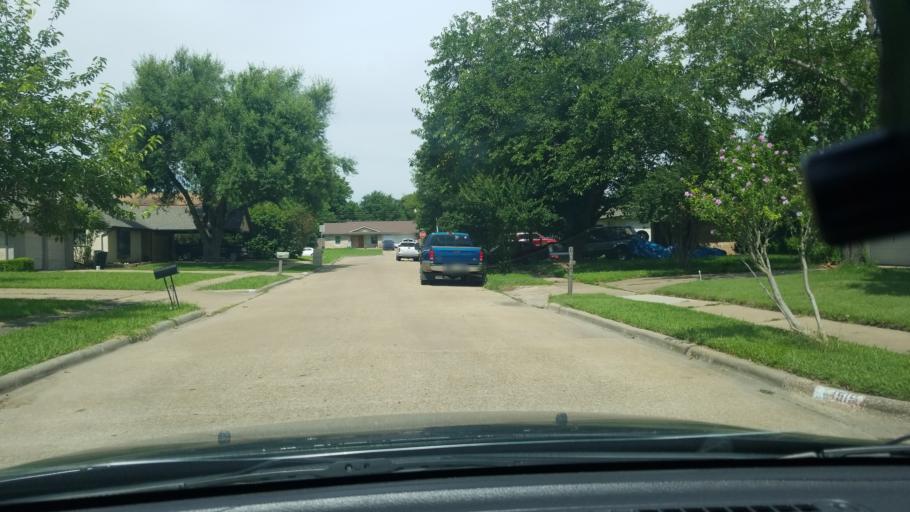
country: US
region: Texas
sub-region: Dallas County
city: Mesquite
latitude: 32.7549
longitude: -96.5778
